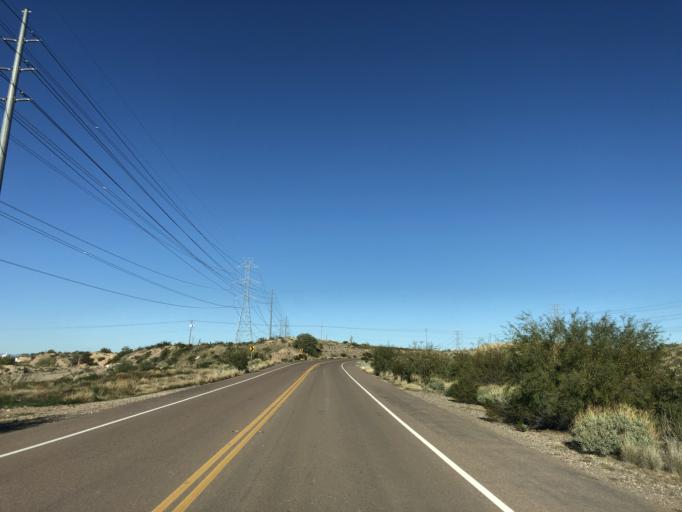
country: US
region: Arizona
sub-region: Maricopa County
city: Sun City West
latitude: 33.6942
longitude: -112.2933
